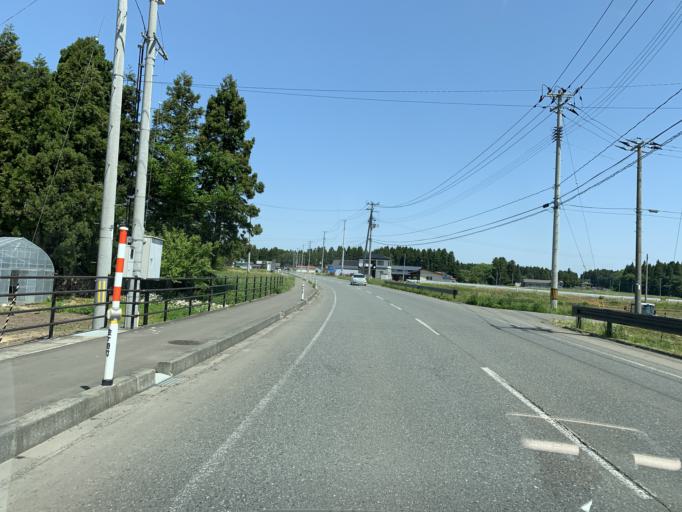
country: JP
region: Iwate
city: Kitakami
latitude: 39.2345
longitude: 141.0670
